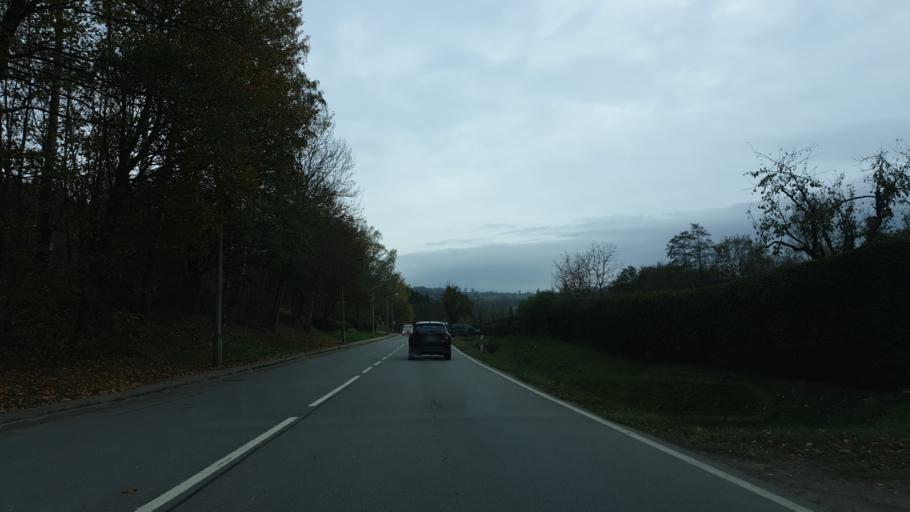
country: DE
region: Saxony
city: Schwarzenberg
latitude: 50.5292
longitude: 12.7869
